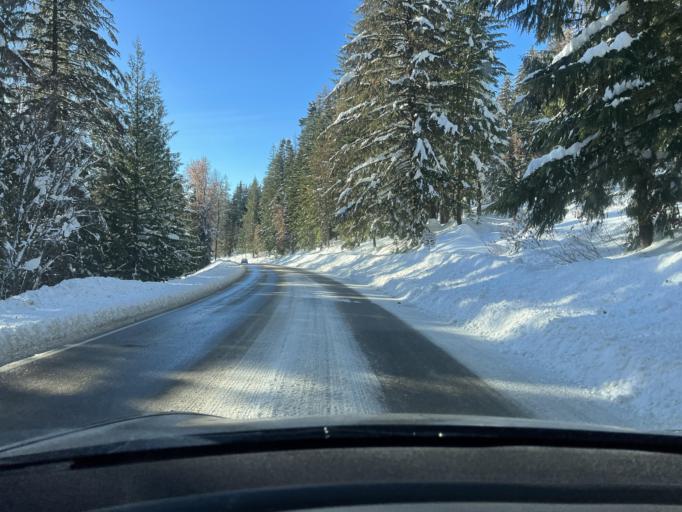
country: US
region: Idaho
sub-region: Bonner County
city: Ponderay
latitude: 48.3444
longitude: -116.5985
